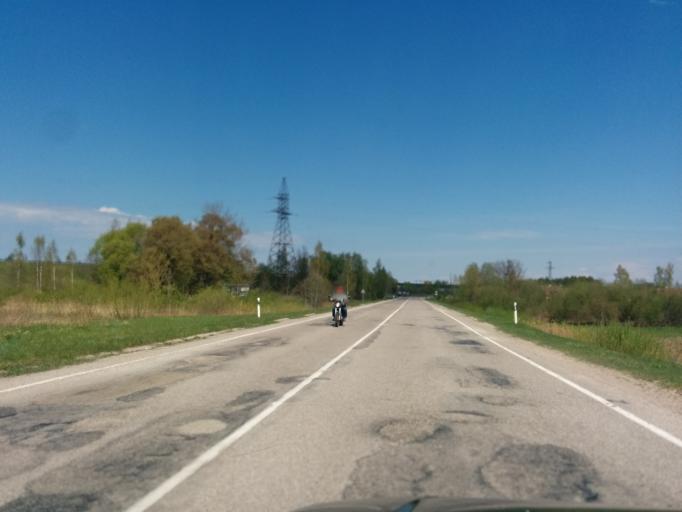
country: LV
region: Ozolnieku
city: Ozolnieki
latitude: 56.6490
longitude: 23.8006
